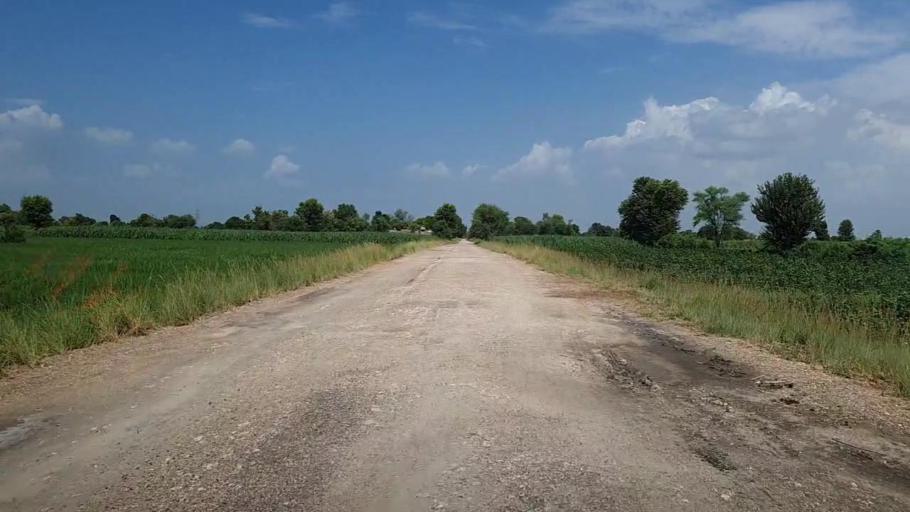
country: PK
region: Sindh
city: Bhiria
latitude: 26.9214
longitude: 68.2089
